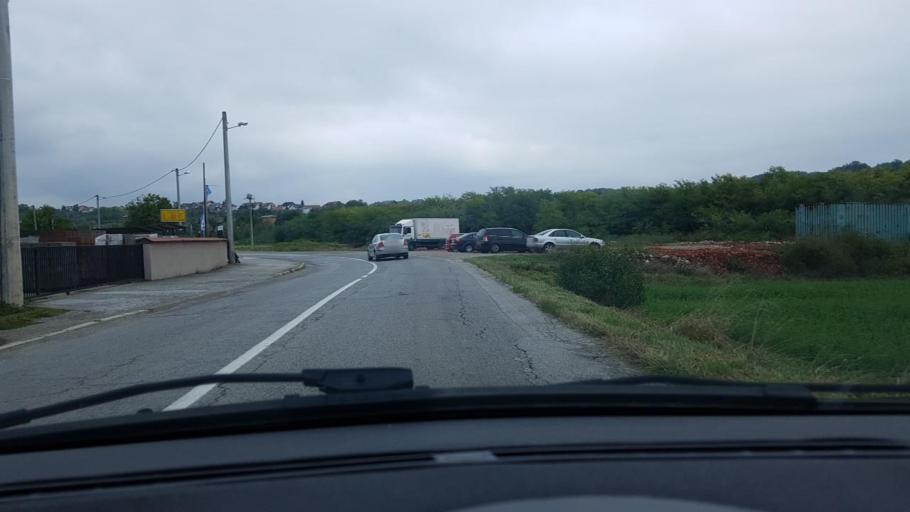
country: HR
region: Grad Zagreb
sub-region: Sesvete
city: Sesvete
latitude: 45.9017
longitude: 16.1258
